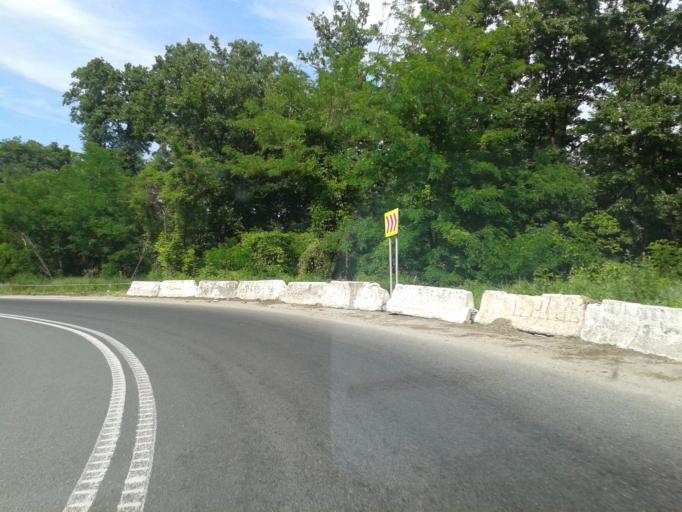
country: RO
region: Hunedoara
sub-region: Comuna Santamaria-Orlea
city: Santamaria-Orlea
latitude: 45.6150
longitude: 22.9849
